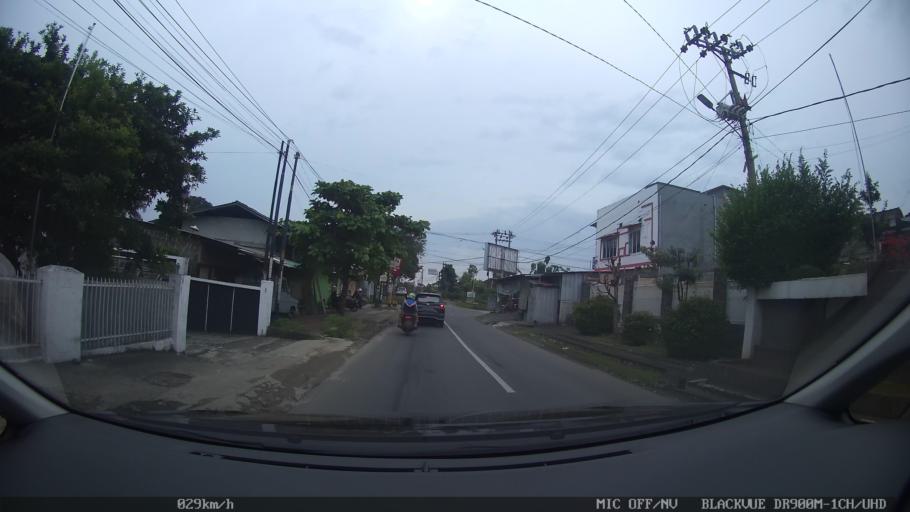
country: ID
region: Lampung
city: Kedaton
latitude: -5.3861
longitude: 105.2490
